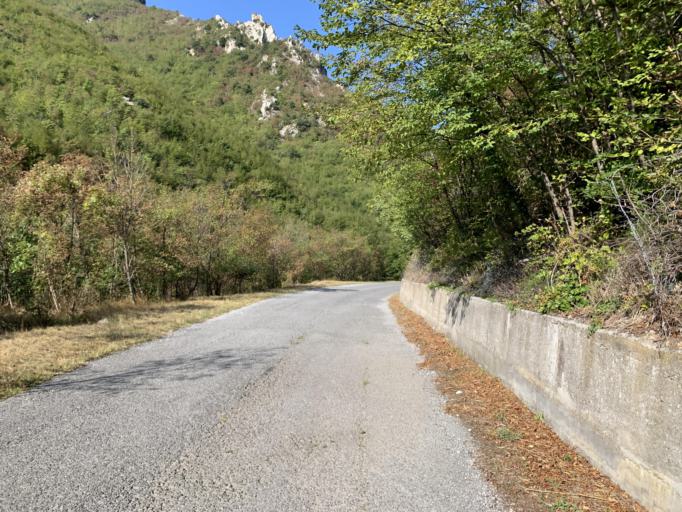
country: IT
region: Liguria
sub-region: Provincia di Savona
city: Magliolo
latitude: 44.1983
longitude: 8.2279
